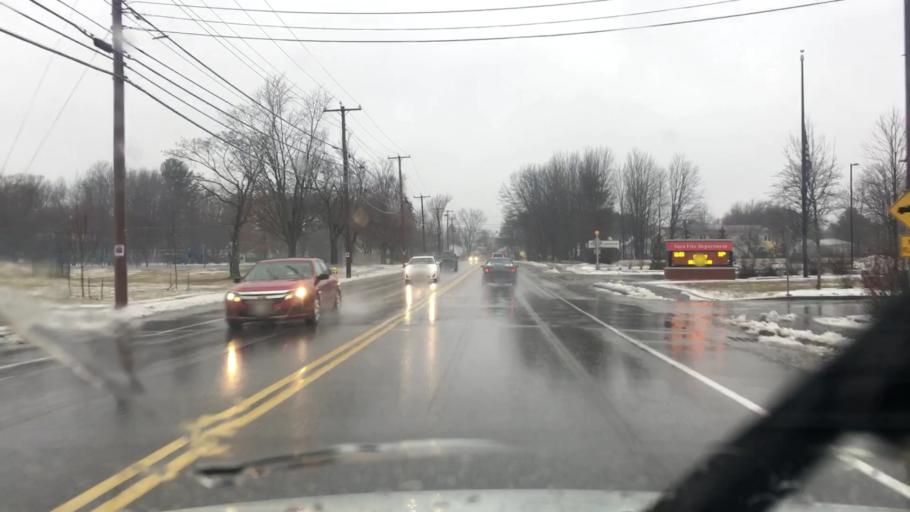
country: US
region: Maine
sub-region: York County
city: Saco
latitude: 43.5124
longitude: -70.4505
